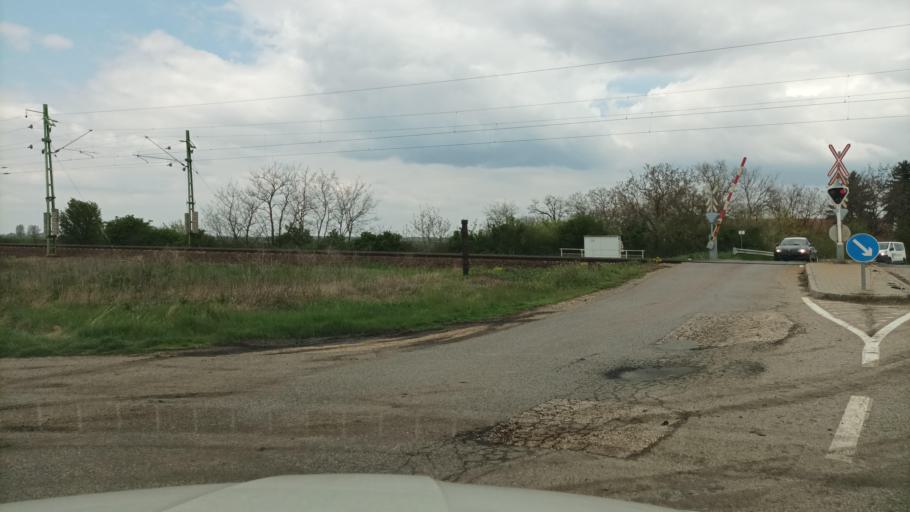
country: HU
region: Pest
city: Abony
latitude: 47.1740
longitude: 19.9884
